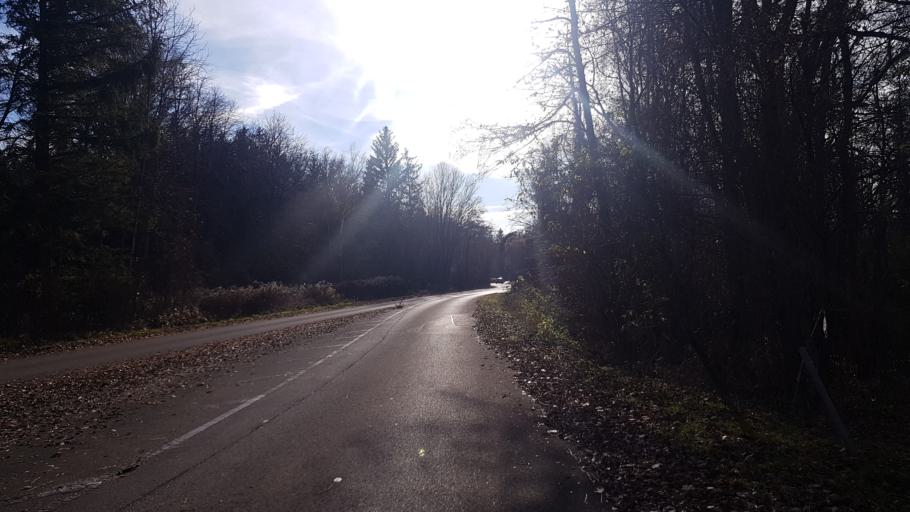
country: DE
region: Bavaria
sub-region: Upper Bavaria
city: Oberschleissheim
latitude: 48.2500
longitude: 11.5279
